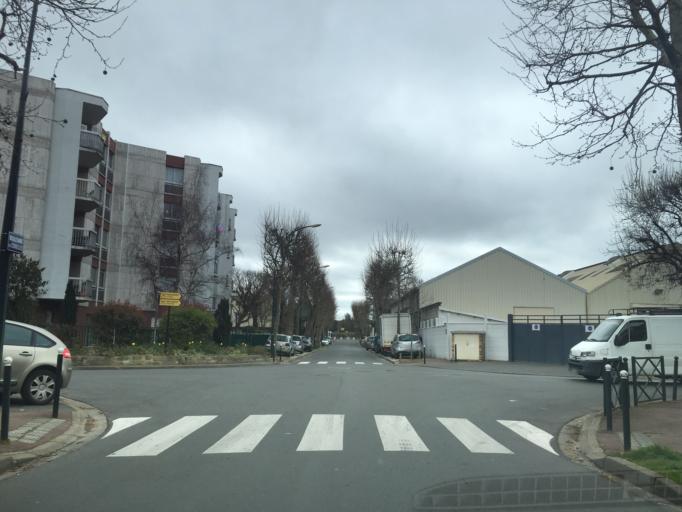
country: FR
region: Ile-de-France
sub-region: Departement du Val-de-Marne
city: Saint-Maur-des-Fosses
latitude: 48.7860
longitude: 2.4922
